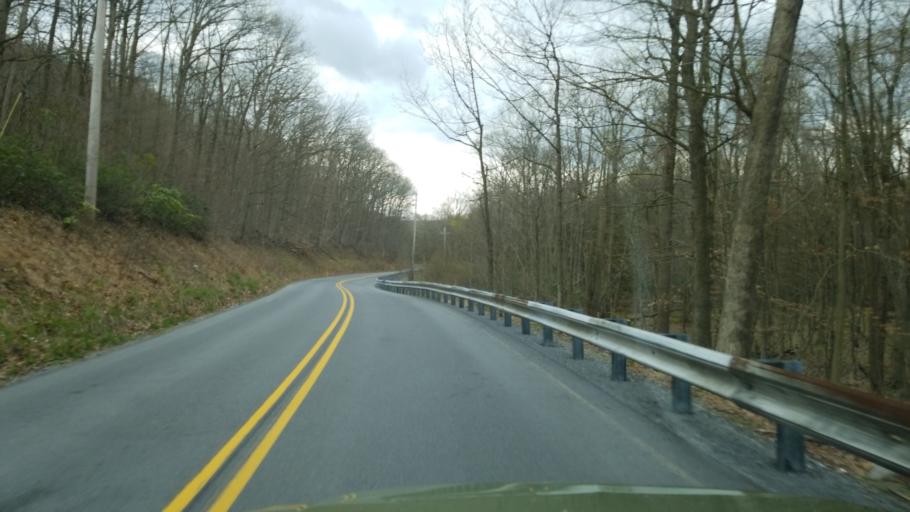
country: US
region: Pennsylvania
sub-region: Blair County
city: Tipton
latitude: 40.6592
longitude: -78.3324
